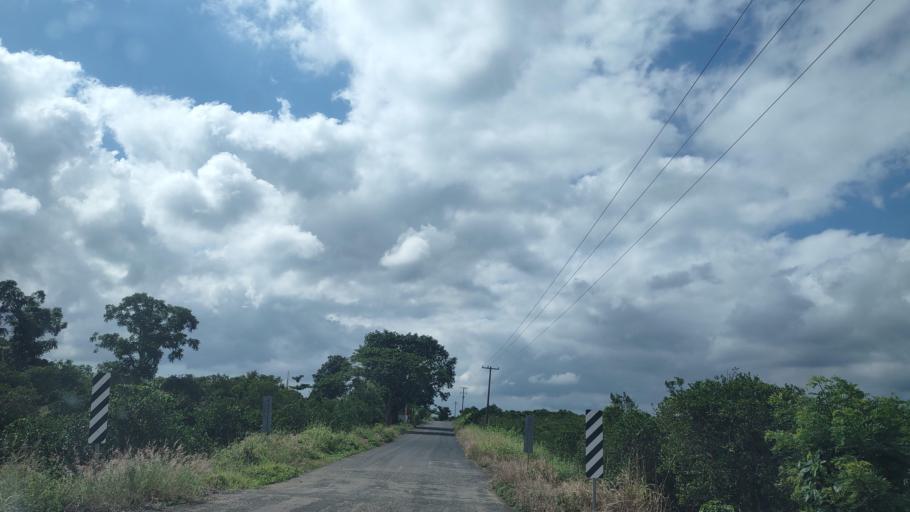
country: MX
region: Puebla
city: San Jose Acateno
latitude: 20.2805
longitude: -97.1311
